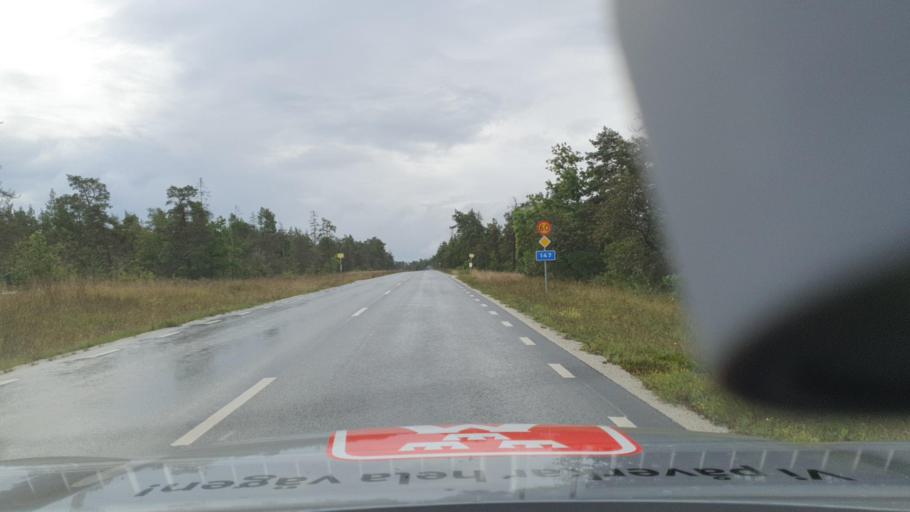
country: SE
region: Gotland
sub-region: Gotland
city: Slite
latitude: 57.7512
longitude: 18.7900
